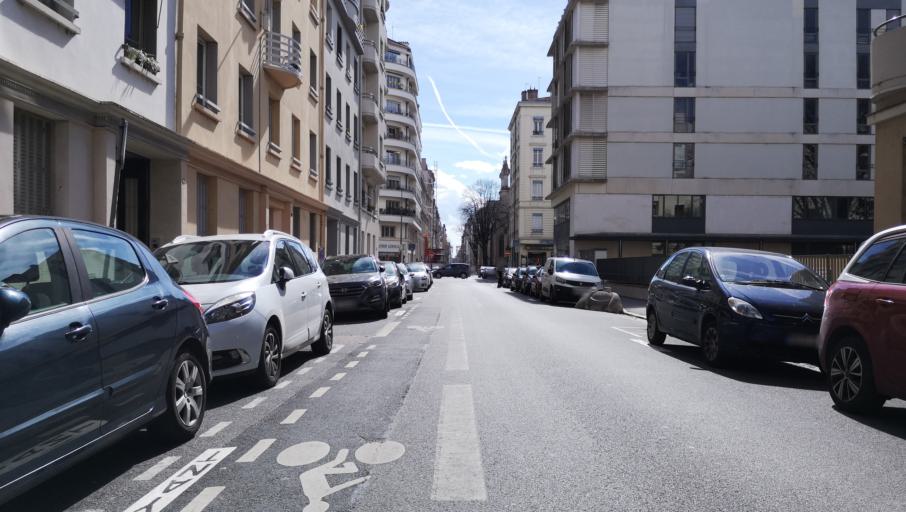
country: FR
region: Rhone-Alpes
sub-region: Departement du Rhone
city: Caluire-et-Cuire
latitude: 45.7733
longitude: 4.8453
